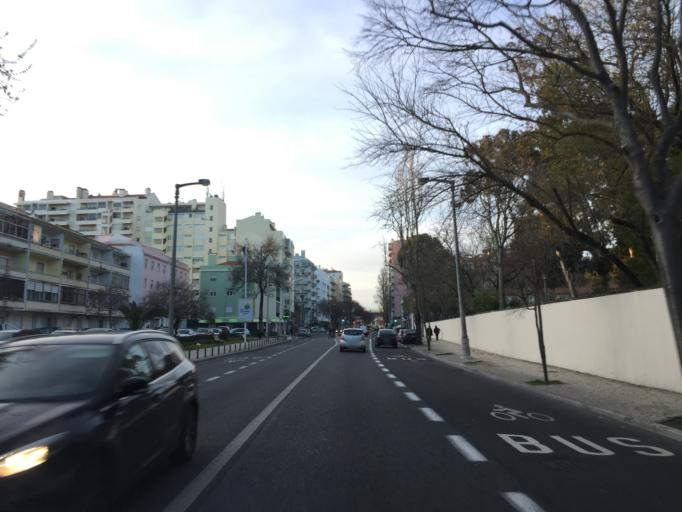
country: PT
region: Lisbon
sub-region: Odivelas
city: Olival do Basto
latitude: 38.7692
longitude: -9.1590
